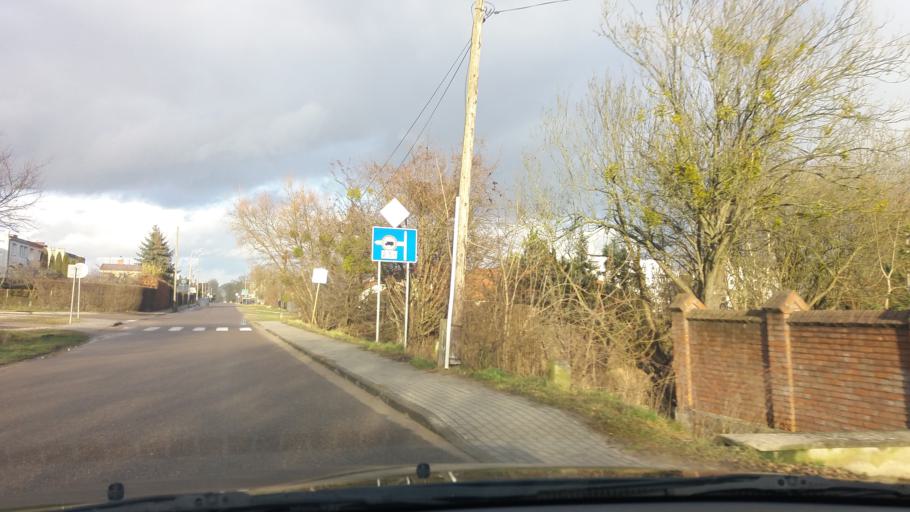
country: PL
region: Warmian-Masurian Voivodeship
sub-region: Powiat szczycienski
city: Szczytno
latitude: 53.5522
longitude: 20.9805
